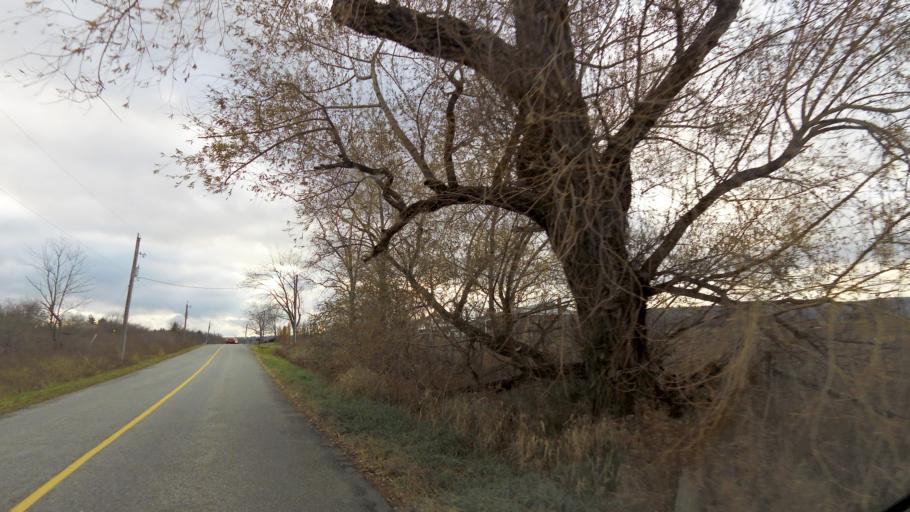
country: CA
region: Ontario
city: Burlington
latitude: 43.4125
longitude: -79.8350
